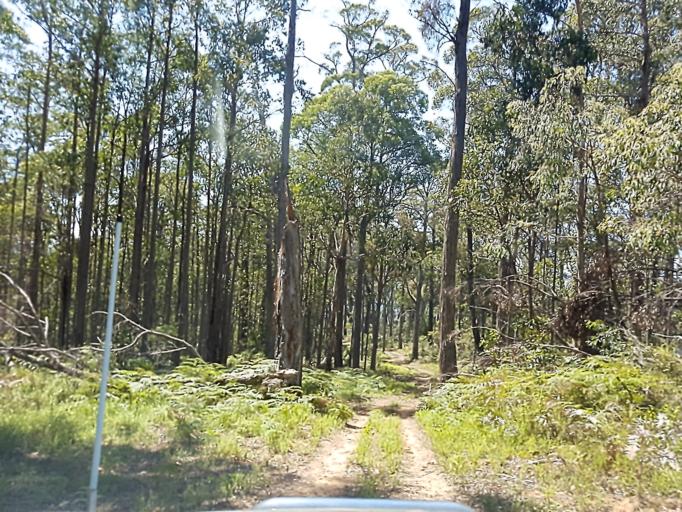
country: AU
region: Victoria
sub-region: East Gippsland
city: Lakes Entrance
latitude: -37.3144
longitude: 148.3364
